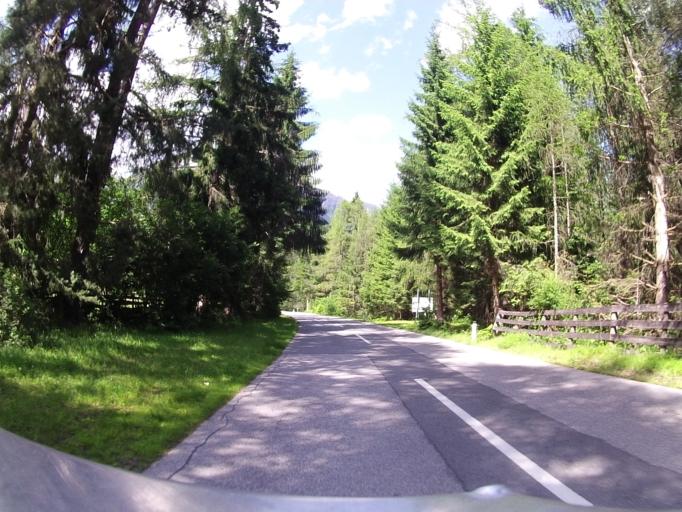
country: AT
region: Tyrol
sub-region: Politischer Bezirk Imst
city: Imst
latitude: 47.2621
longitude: 10.7394
